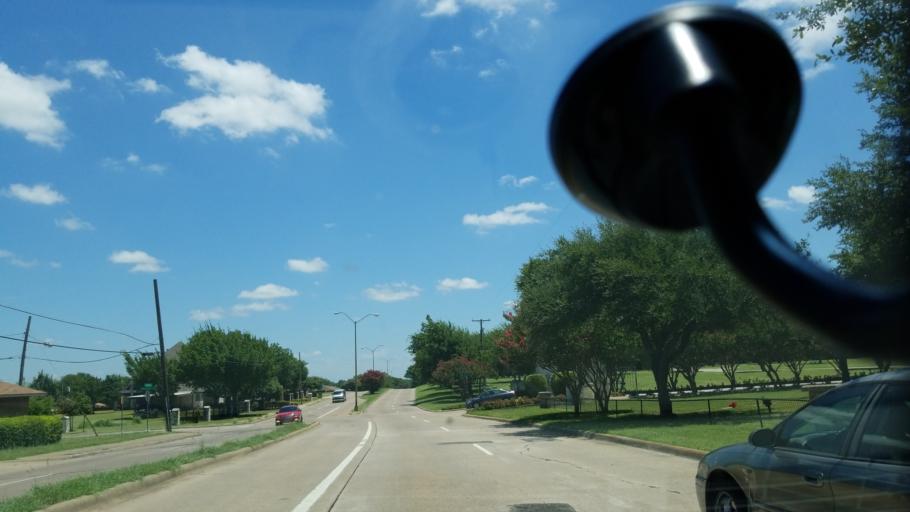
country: US
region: Texas
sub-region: Dallas County
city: Cockrell Hill
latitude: 32.6750
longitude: -96.8155
